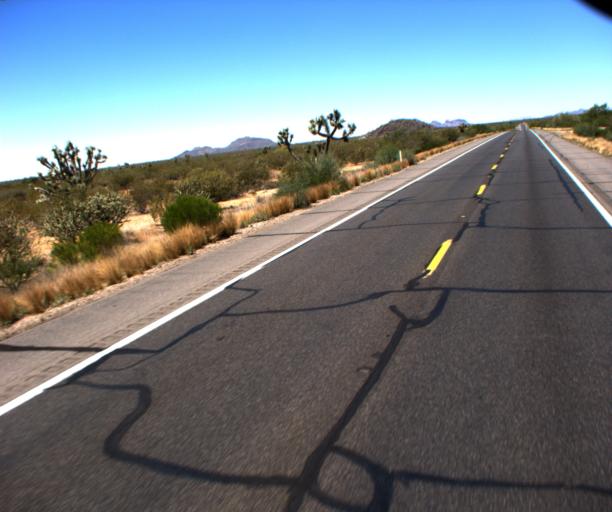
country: US
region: Arizona
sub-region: Yavapai County
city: Congress
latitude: 34.1654
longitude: -113.0110
